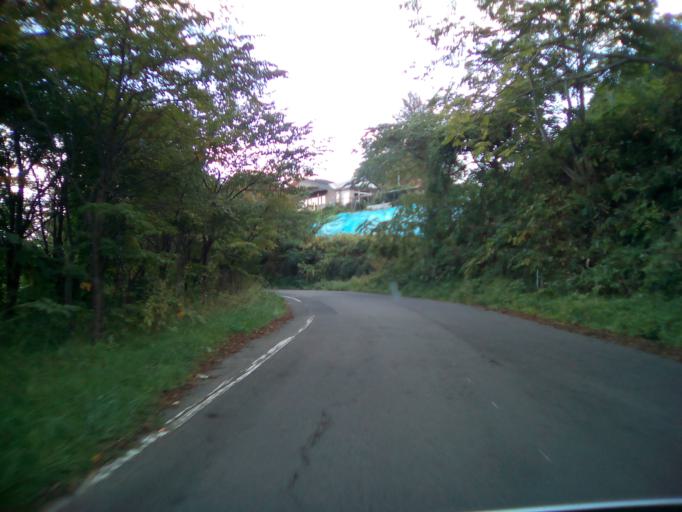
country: JP
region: Hokkaido
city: Date
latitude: 42.5844
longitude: 140.7946
